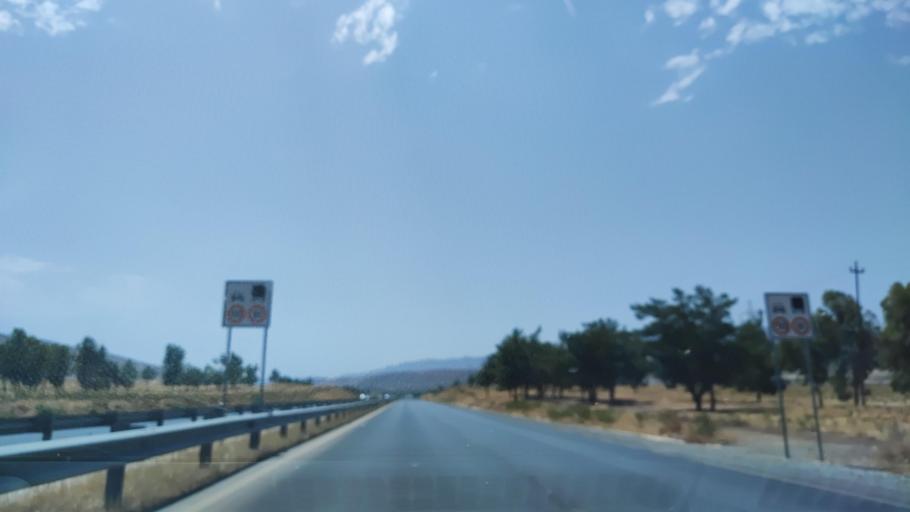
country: IQ
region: Arbil
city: Shaqlawah
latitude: 36.4687
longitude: 44.3824
